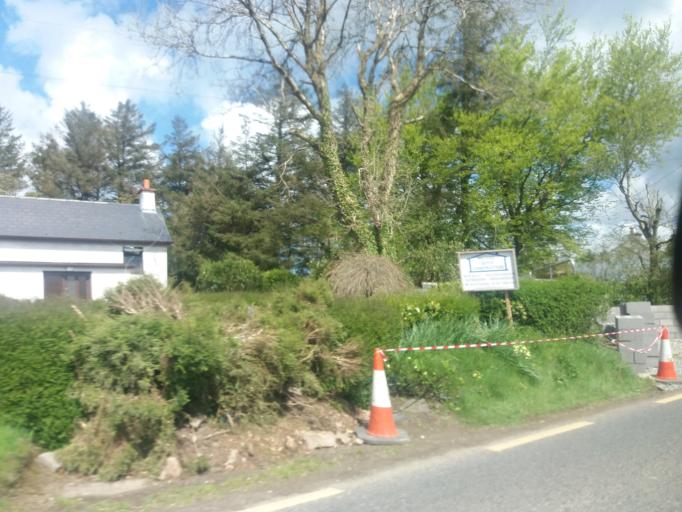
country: IE
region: Leinster
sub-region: Loch Garman
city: Loch Garman
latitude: 52.2995
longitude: -6.5641
